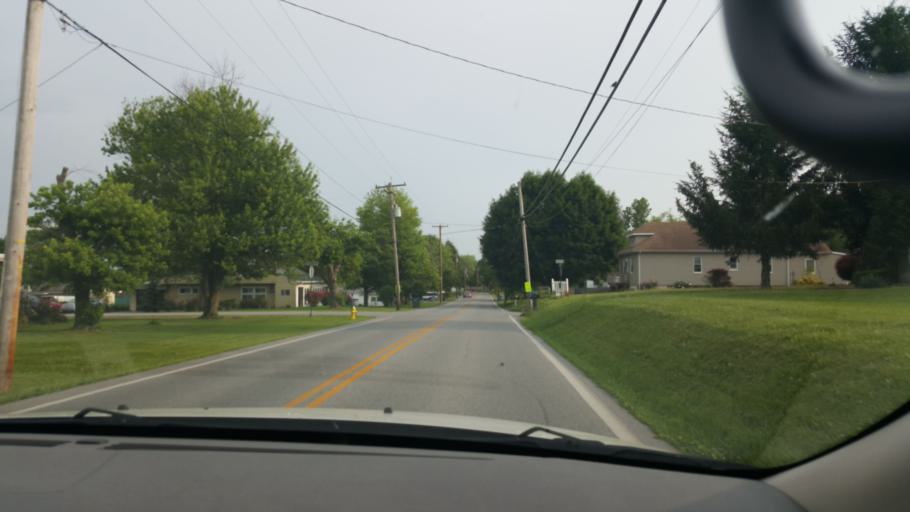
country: US
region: Pennsylvania
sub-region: York County
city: Weigelstown
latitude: 39.9945
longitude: -76.8126
